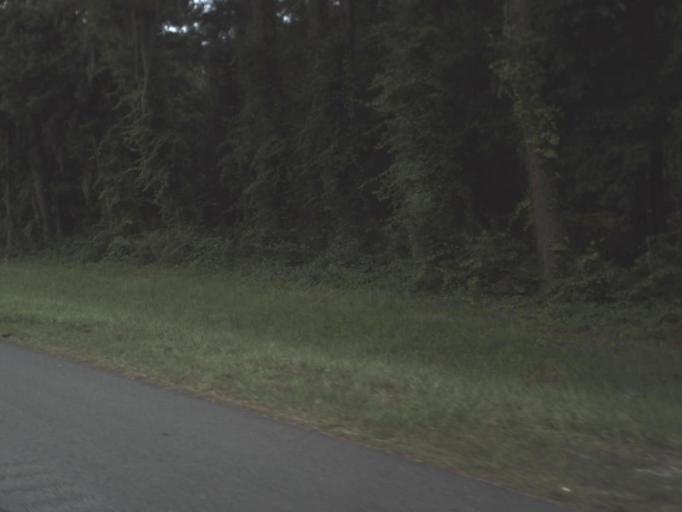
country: US
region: Florida
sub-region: Hamilton County
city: Jasper
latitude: 30.3947
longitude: -82.8804
